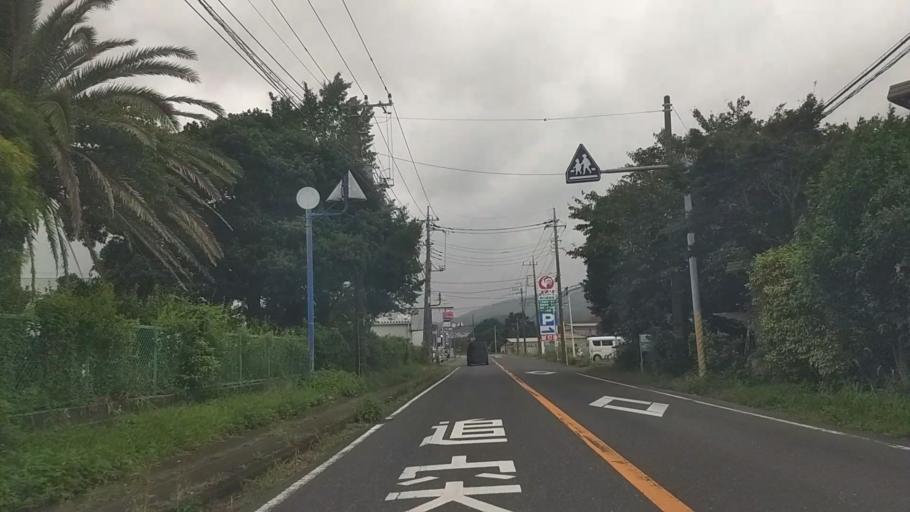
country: JP
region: Chiba
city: Kawaguchi
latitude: 35.1345
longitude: 140.0041
